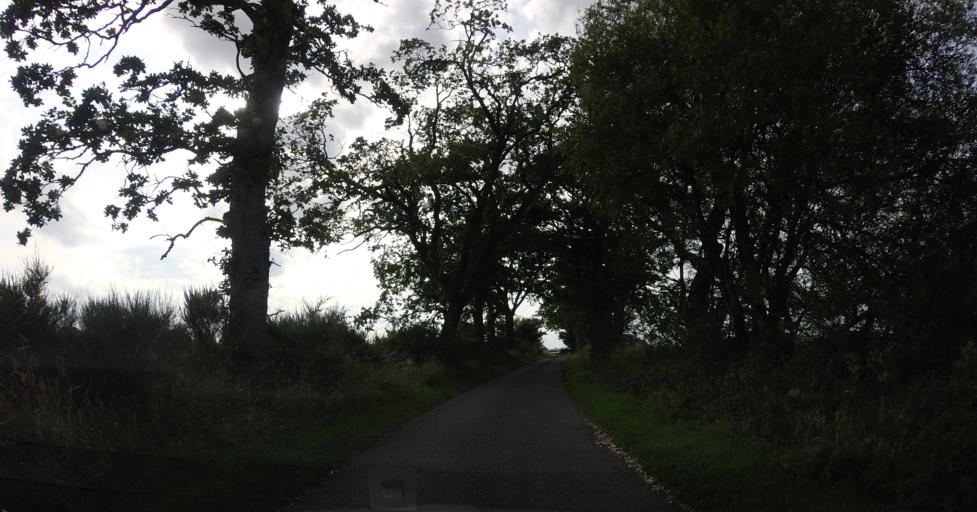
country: GB
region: Scotland
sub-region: Perth and Kinross
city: Auchterarder
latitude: 56.3004
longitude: -3.7589
